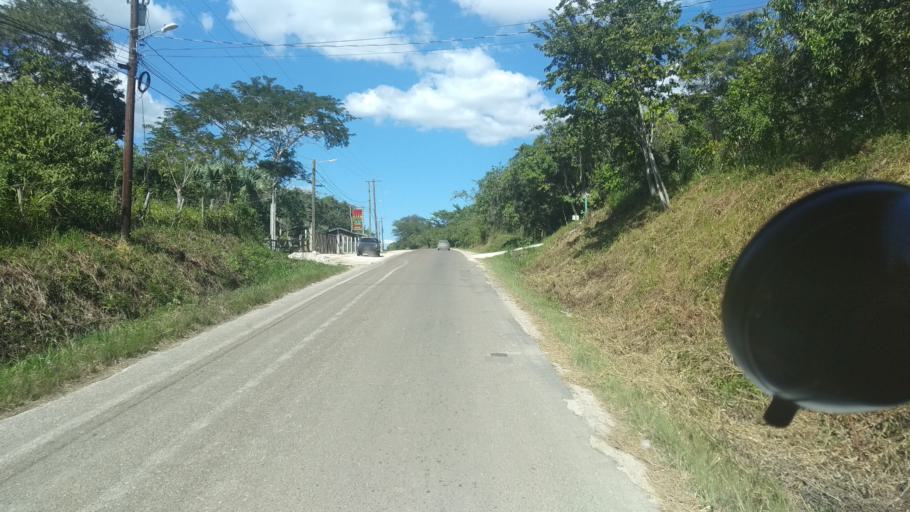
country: BZ
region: Cayo
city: Benque Viejo del Carmen
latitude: 17.0910
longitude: -89.1233
